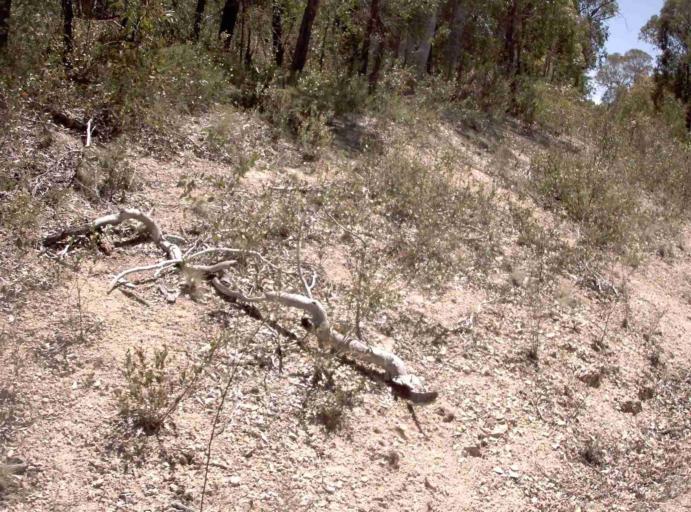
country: AU
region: New South Wales
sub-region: Snowy River
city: Jindabyne
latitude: -37.1148
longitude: 148.2458
